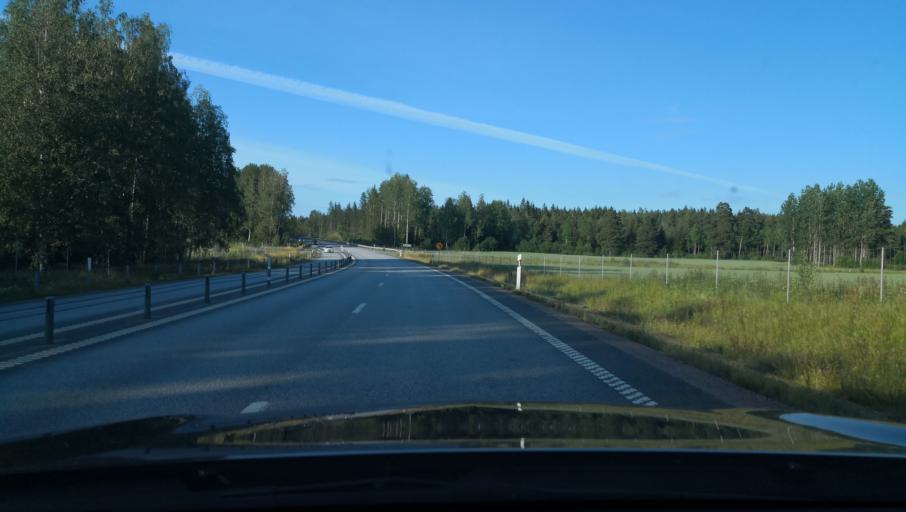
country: SE
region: Uppsala
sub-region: Uppsala Kommun
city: Vattholma
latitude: 59.9711
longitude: 17.9329
